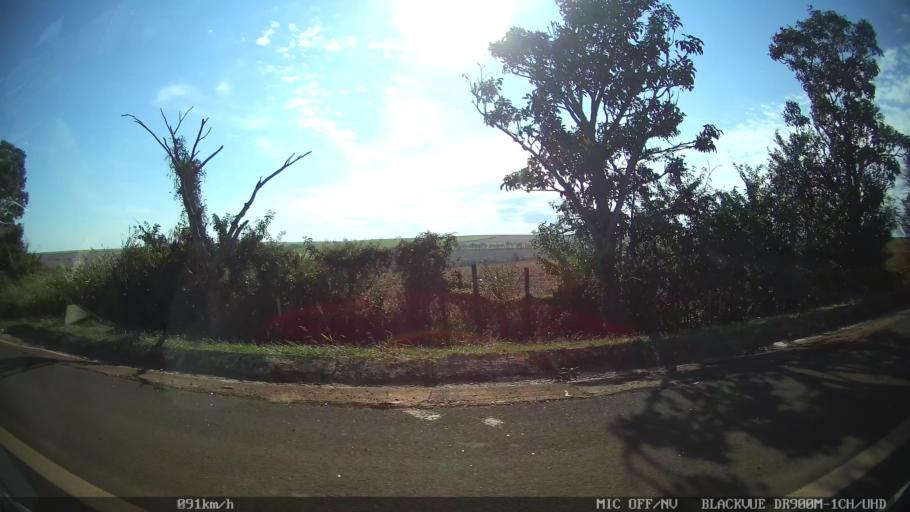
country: BR
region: Sao Paulo
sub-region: Iracemapolis
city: Iracemapolis
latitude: -22.6720
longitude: -47.5565
